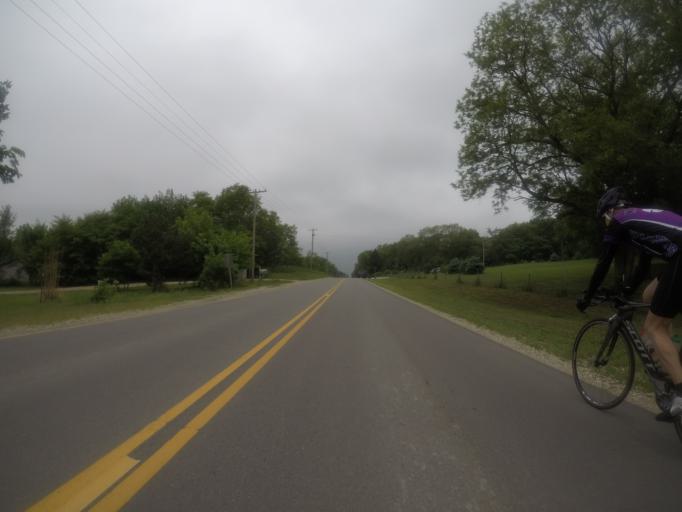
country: US
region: Kansas
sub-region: Riley County
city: Manhattan
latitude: 39.1959
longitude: -96.4391
